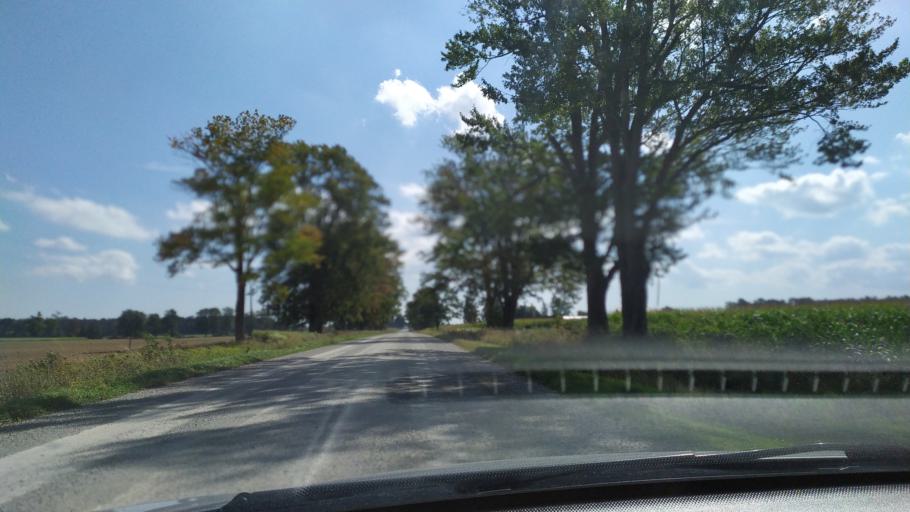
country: CA
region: Ontario
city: Stratford
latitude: 43.2848
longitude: -80.9287
